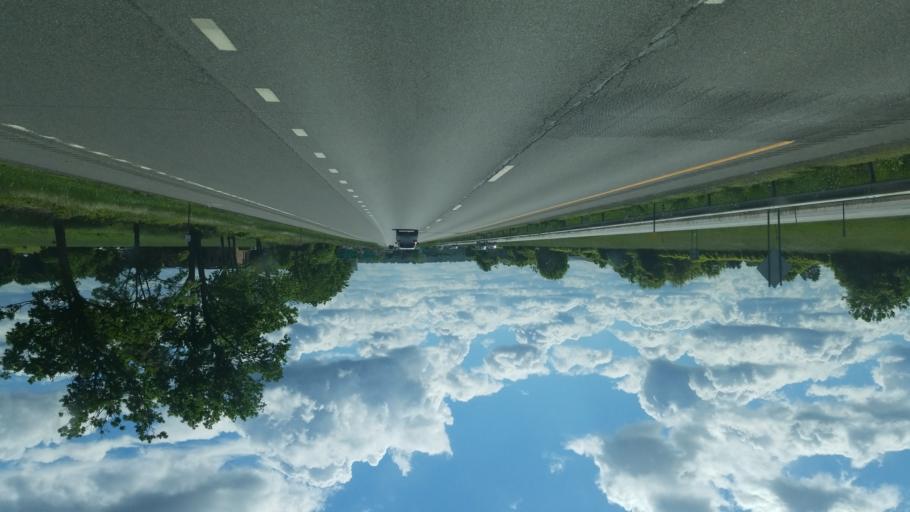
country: US
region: New York
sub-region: Onondaga County
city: Galeville
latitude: 43.0995
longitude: -76.1771
